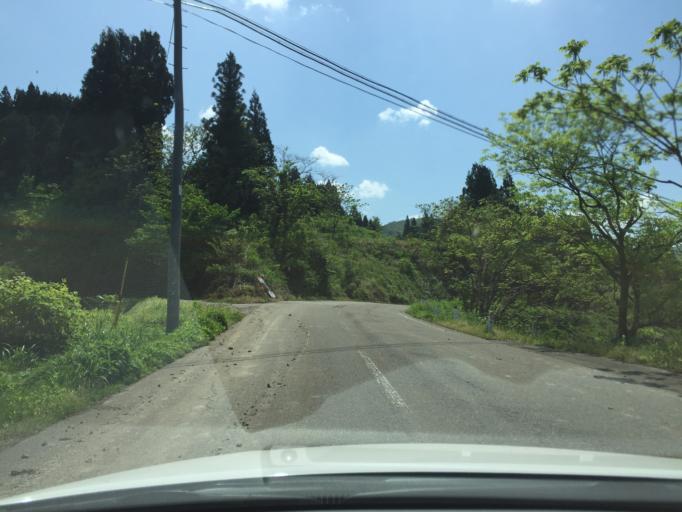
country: JP
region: Niigata
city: Tochio-honcho
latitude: 37.4782
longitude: 139.0493
